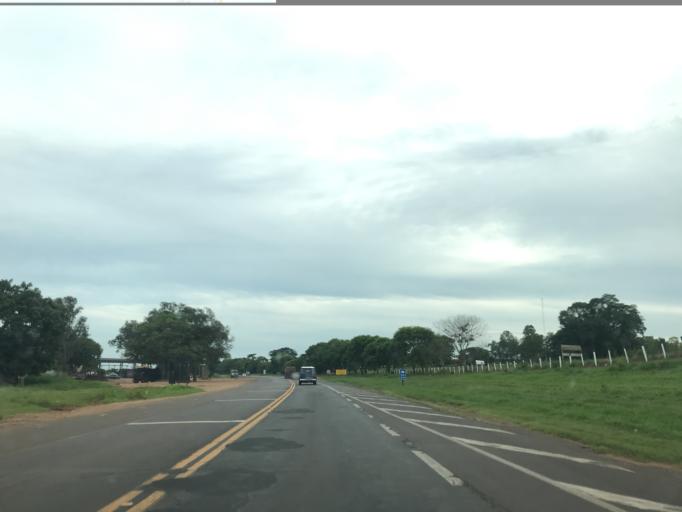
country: BR
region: Sao Paulo
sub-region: Tupa
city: Tupa
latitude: -21.6416
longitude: -50.4989
